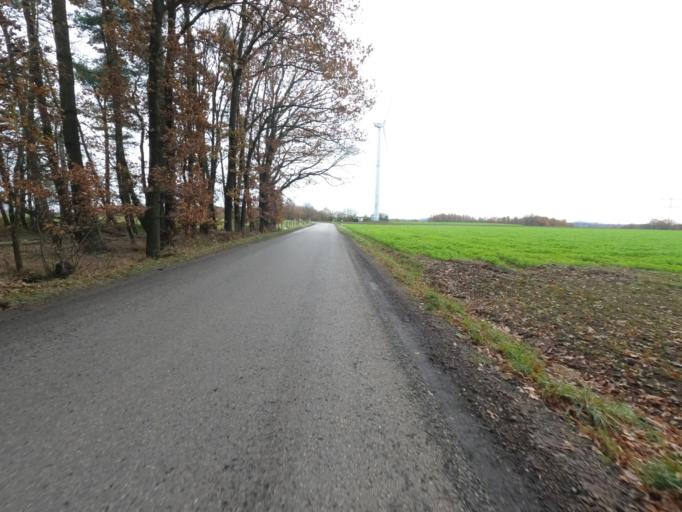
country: DE
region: North Rhine-Westphalia
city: Geilenkirchen
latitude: 50.9844
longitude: 6.1365
